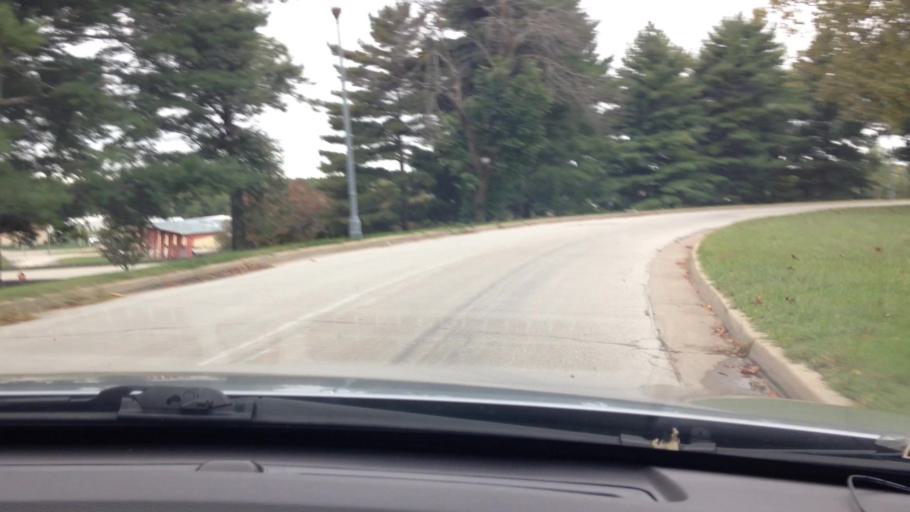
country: US
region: Kansas
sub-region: Leavenworth County
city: Lansing
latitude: 39.2752
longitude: -94.8933
